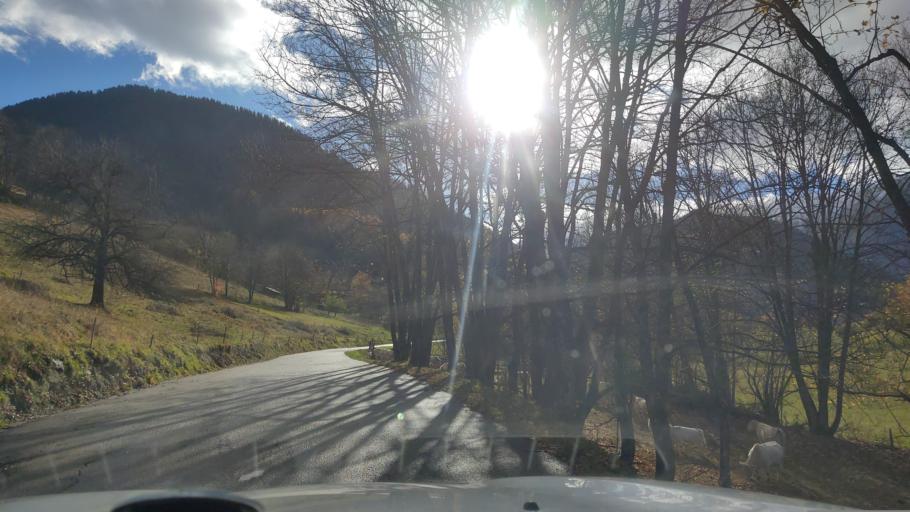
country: FR
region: Rhone-Alpes
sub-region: Departement de la Savoie
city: Saint-Jean-de-Maurienne
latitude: 45.2205
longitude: 6.3186
